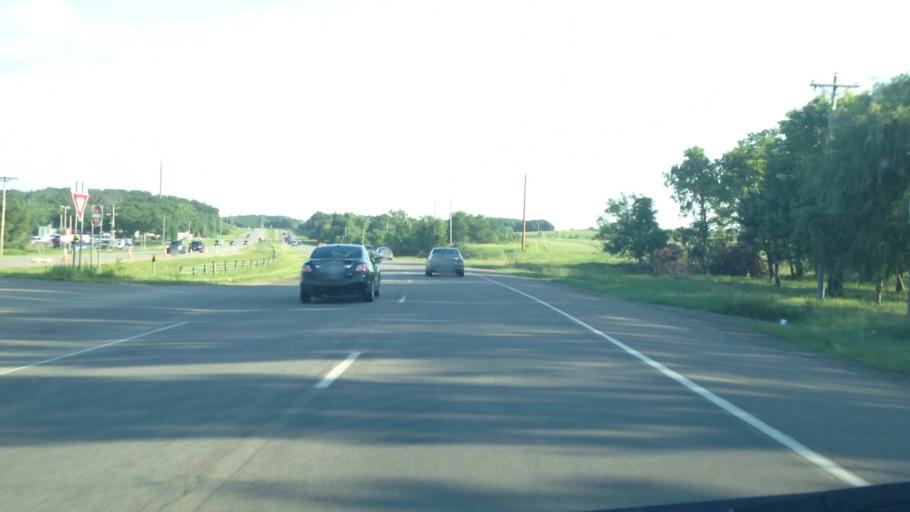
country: US
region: Minnesota
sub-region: Sherburne County
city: Elk River
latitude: 45.3675
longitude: -93.5649
